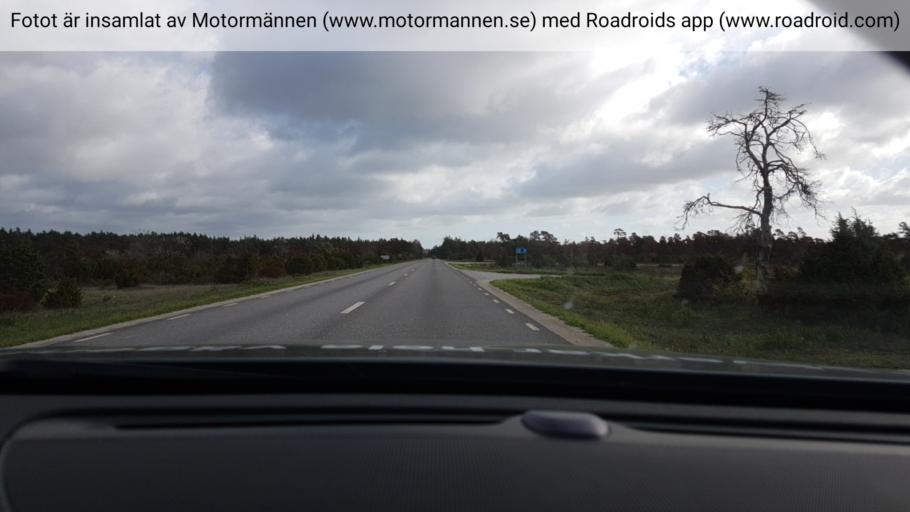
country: SE
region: Gotland
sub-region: Gotland
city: Visby
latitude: 57.6625
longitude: 18.4445
